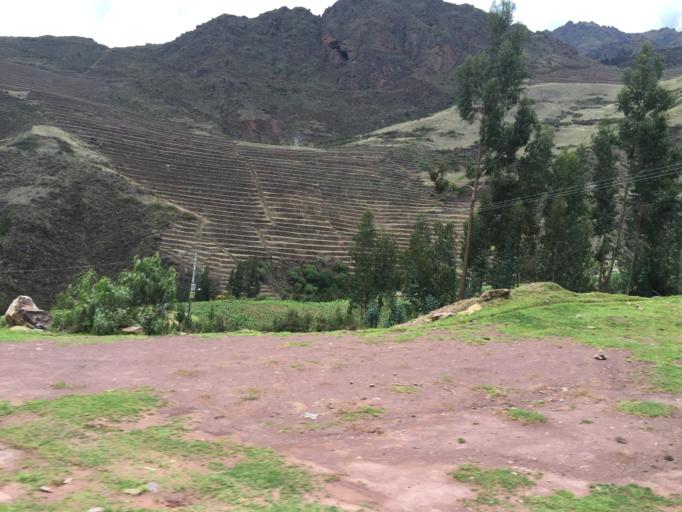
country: PE
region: Cusco
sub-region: Provincia de Calca
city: Pisac
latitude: -13.4128
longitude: -71.8360
